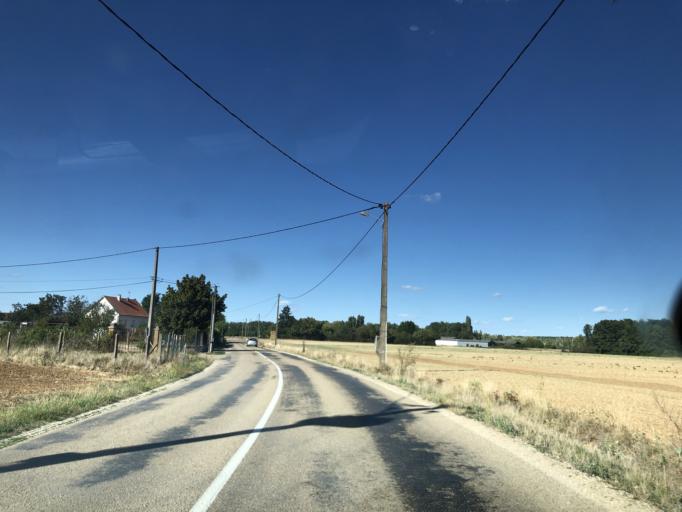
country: FR
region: Bourgogne
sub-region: Departement de l'Yonne
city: Appoigny
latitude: 47.8803
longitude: 3.5407
